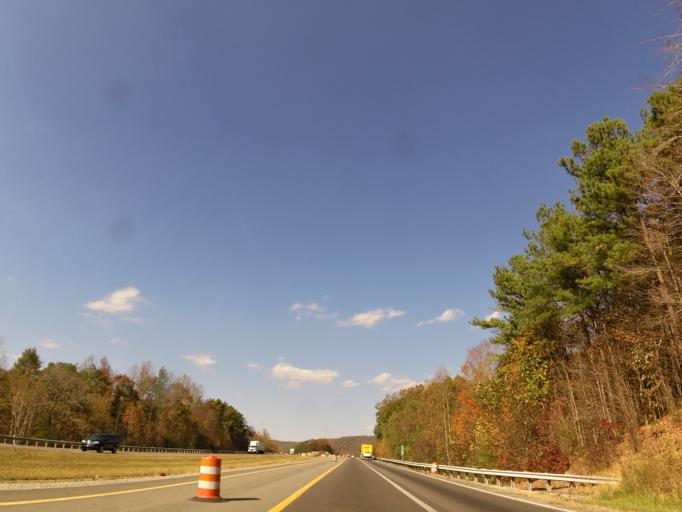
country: US
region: Tennessee
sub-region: Campbell County
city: Jacksboro
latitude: 36.3529
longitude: -84.2305
